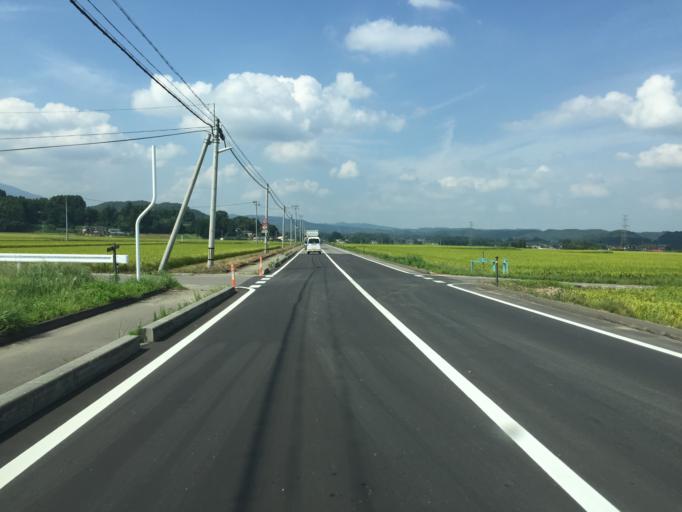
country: JP
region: Fukushima
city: Motomiya
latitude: 37.5492
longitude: 140.3841
